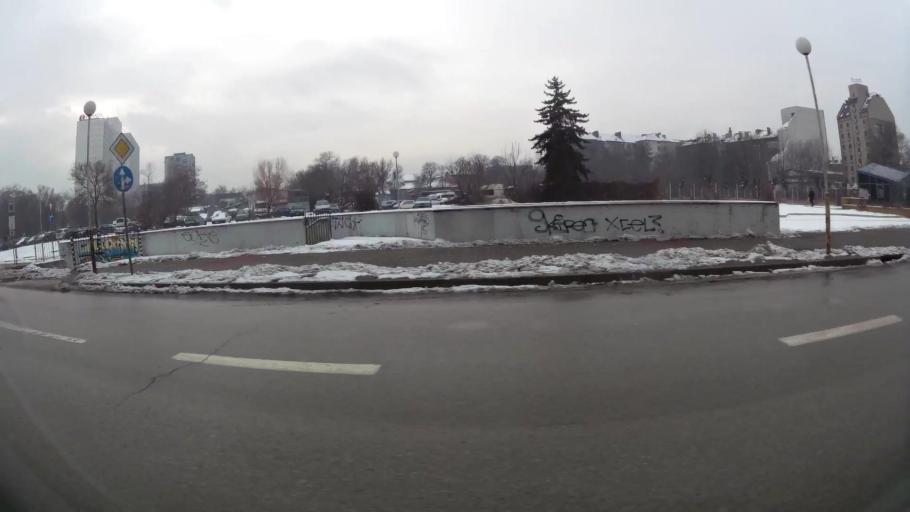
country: BG
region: Sofia-Capital
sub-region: Stolichna Obshtina
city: Sofia
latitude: 42.7107
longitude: 23.3206
